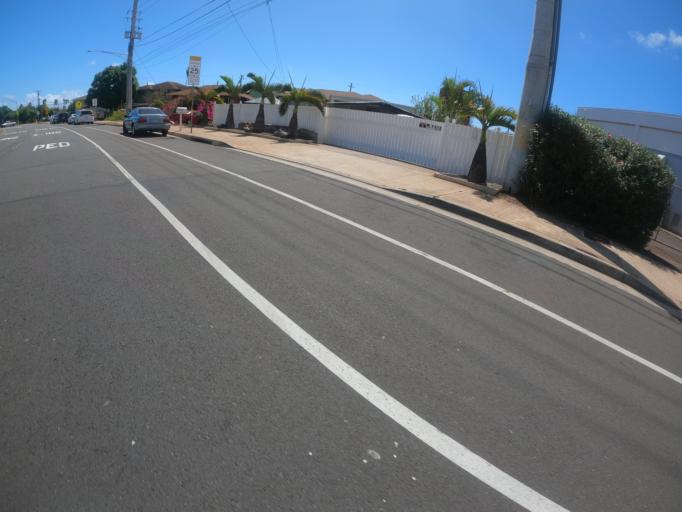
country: US
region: Hawaii
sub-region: Honolulu County
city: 'Ewa Beach
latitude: 21.3119
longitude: -158.0096
